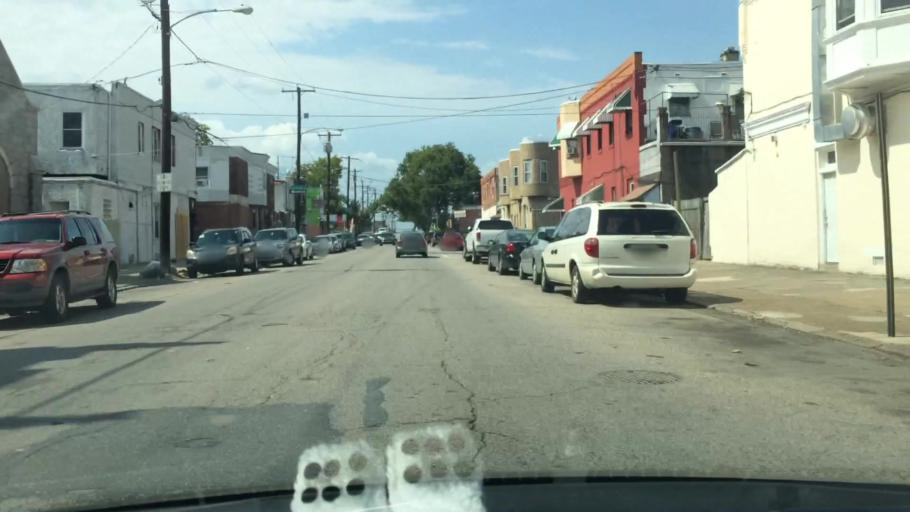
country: US
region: Pennsylvania
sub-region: Delaware County
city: Colwyn
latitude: 39.9241
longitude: -75.2278
